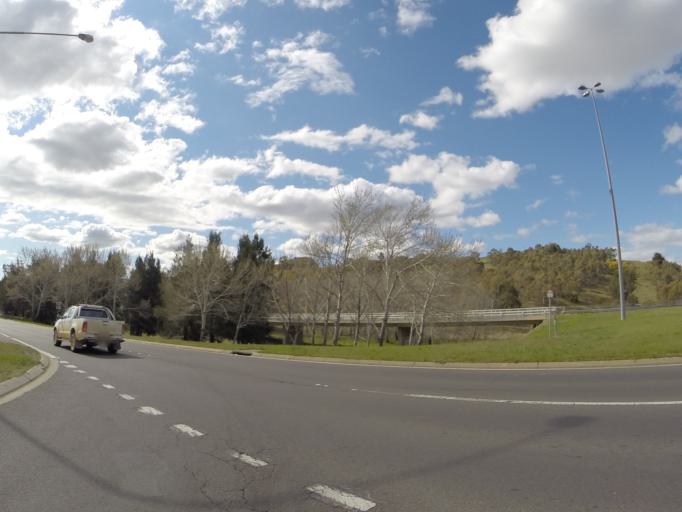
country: AU
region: Australian Capital Territory
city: Belconnen
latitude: -35.2013
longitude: 149.0941
